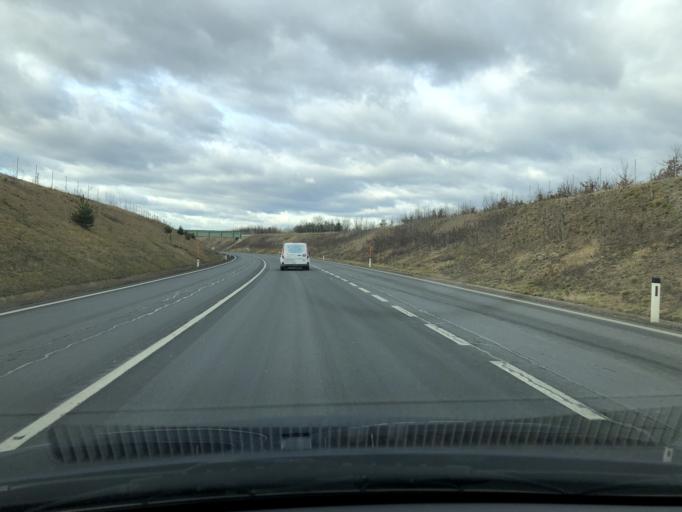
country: AT
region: Burgenland
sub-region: Politischer Bezirk Oberwart
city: Schachendorf
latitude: 47.2760
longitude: 16.4408
